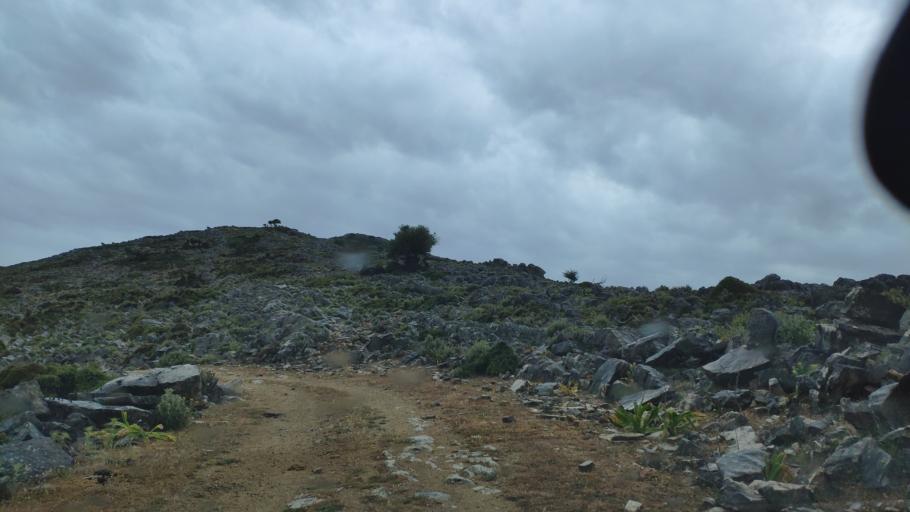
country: GR
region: West Greece
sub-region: Nomos Aitolias kai Akarnanias
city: Archontochorion
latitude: 38.6767
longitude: 21.0146
